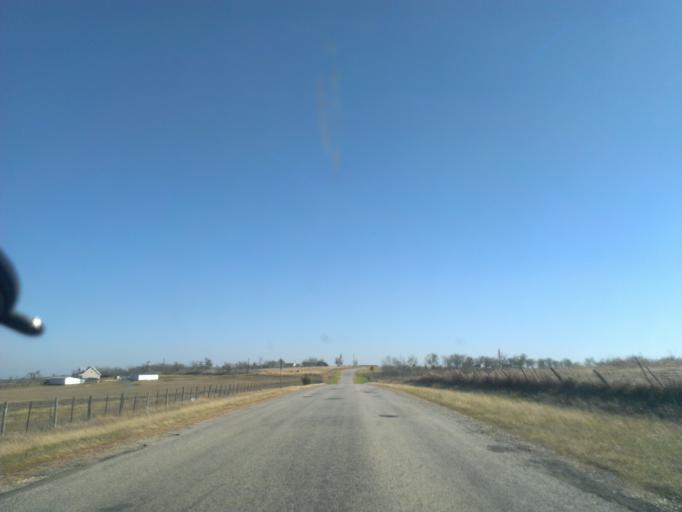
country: US
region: Texas
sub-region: Williamson County
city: Taylor
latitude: 30.5768
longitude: -97.3145
